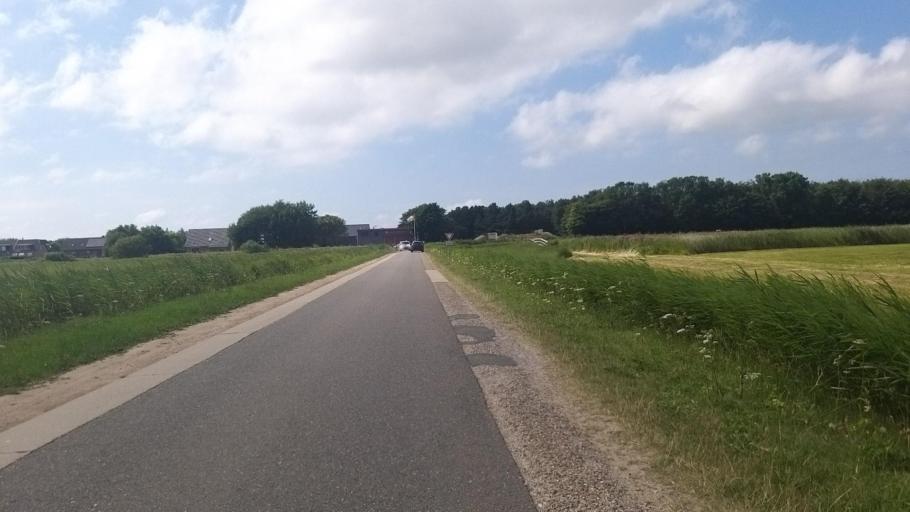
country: NL
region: North Holland
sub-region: Gemeente Texel
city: Den Burg
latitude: 53.1461
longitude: 4.8631
